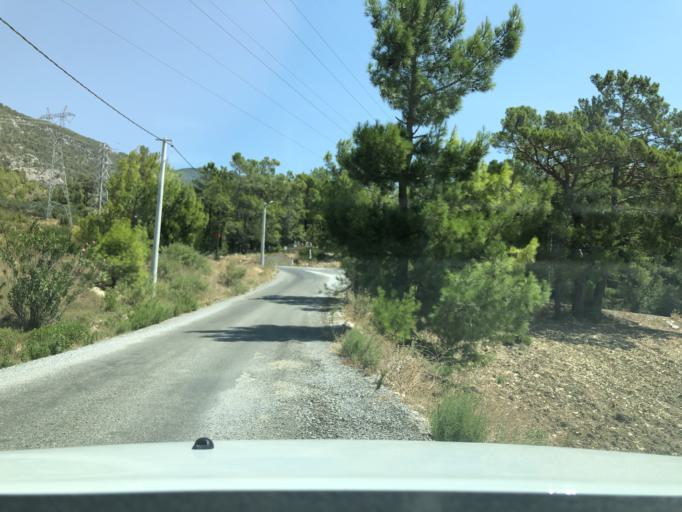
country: TR
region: Antalya
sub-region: Manavgat
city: Manavgat
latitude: 36.8762
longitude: 31.5489
